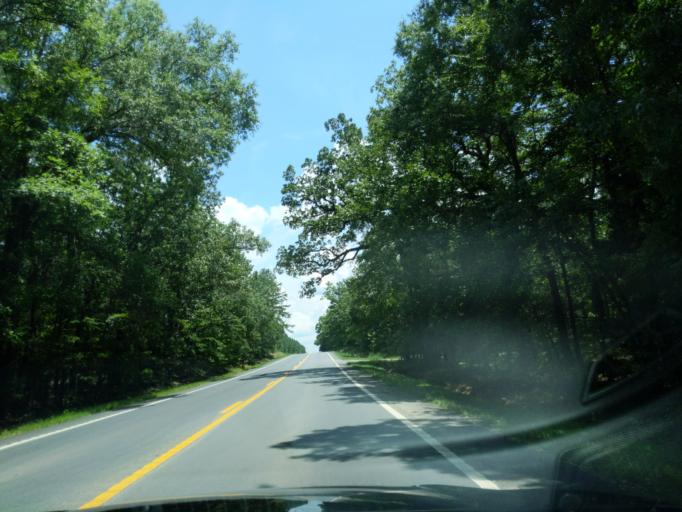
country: US
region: South Carolina
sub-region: Edgefield County
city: Edgefield
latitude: 33.8470
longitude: -81.9782
